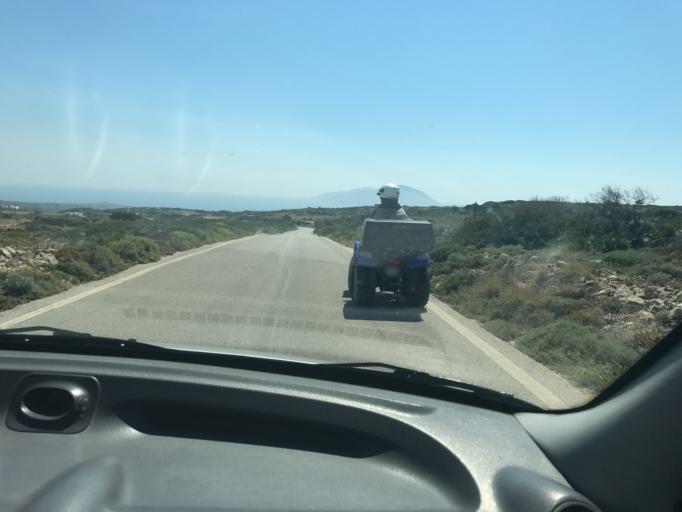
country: GR
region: South Aegean
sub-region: Nomos Dodekanisou
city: Karpathos
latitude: 35.4793
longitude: 27.1425
